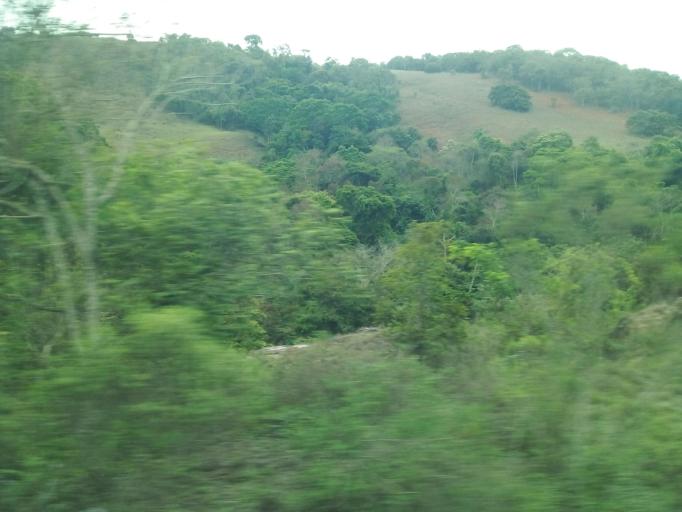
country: BR
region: Minas Gerais
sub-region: Nova Era
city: Nova Era
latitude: -19.7232
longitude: -42.9692
